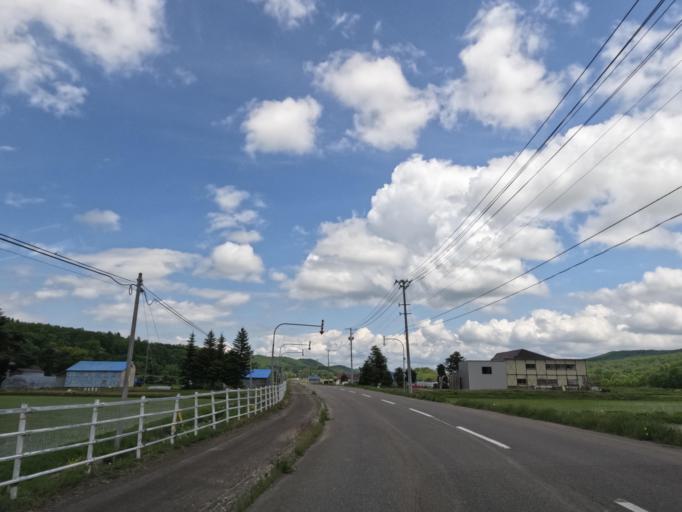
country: JP
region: Hokkaido
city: Takikawa
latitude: 43.5861
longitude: 141.7720
